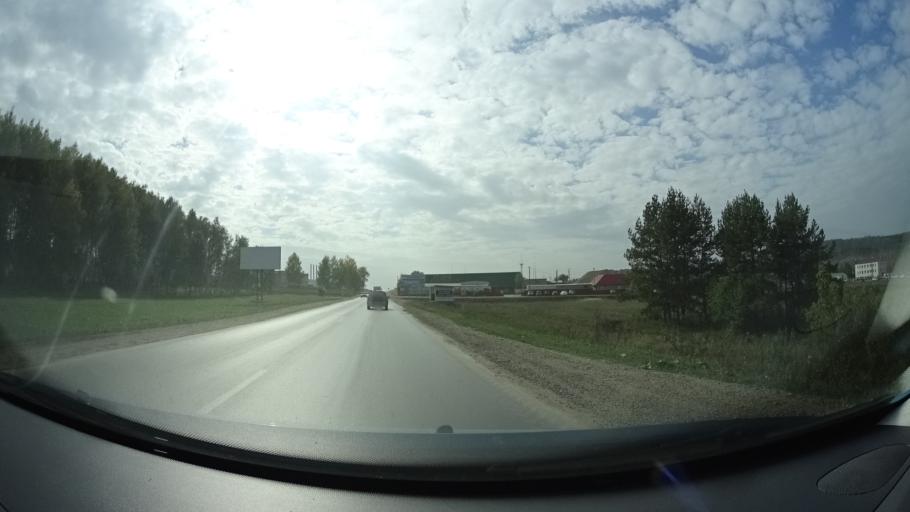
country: RU
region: Bashkortostan
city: Oktyabr'skiy
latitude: 54.5213
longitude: 53.5408
